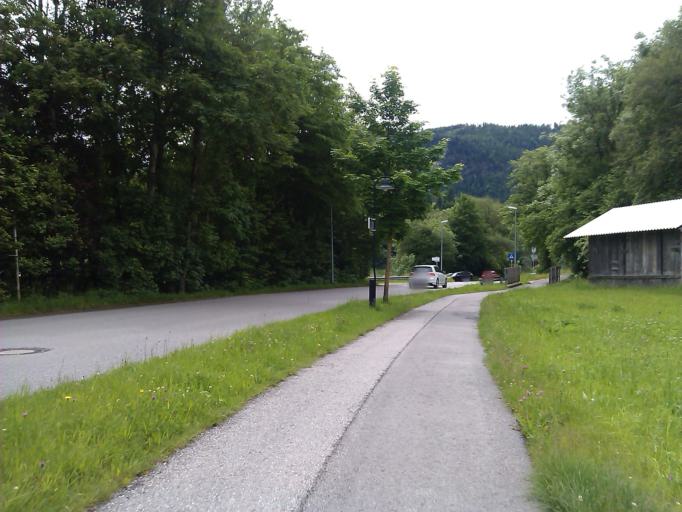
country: AT
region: Tyrol
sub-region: Politischer Bezirk Reutte
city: Reutte
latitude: 47.4773
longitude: 10.7230
